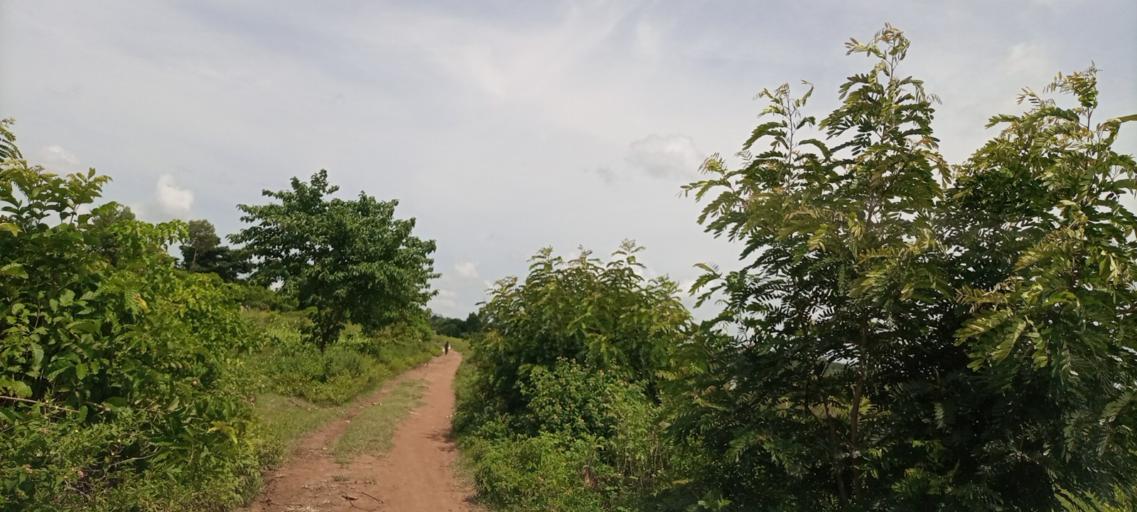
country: UG
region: Eastern Region
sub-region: Budaka District
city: Budaka
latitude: 1.1727
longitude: 33.9512
